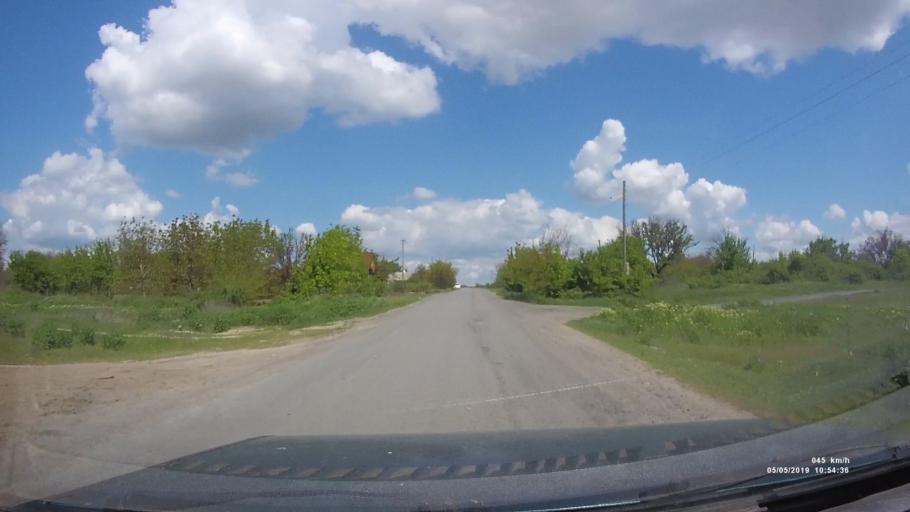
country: RU
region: Rostov
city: Ust'-Donetskiy
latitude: 47.6594
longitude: 40.8227
